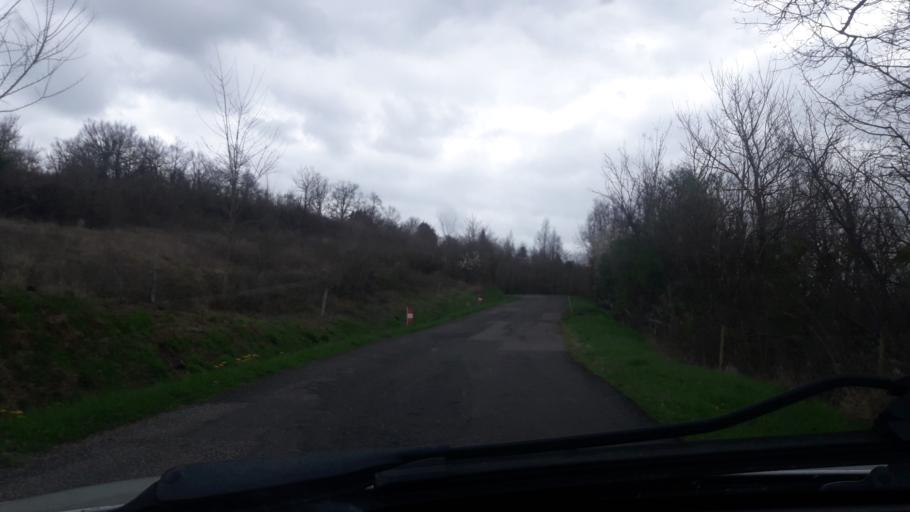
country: FR
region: Midi-Pyrenees
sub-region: Departement de la Haute-Garonne
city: Montesquieu-Volvestre
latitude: 43.2302
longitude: 1.2856
